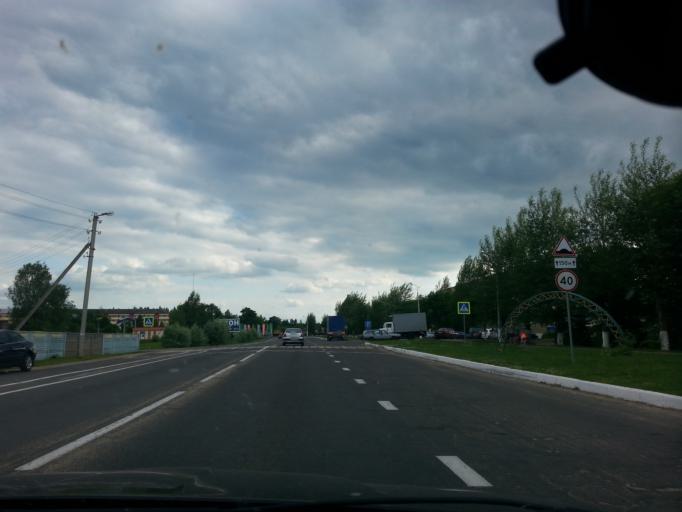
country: BY
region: Minsk
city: Myadzyel
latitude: 54.8695
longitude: 26.9356
